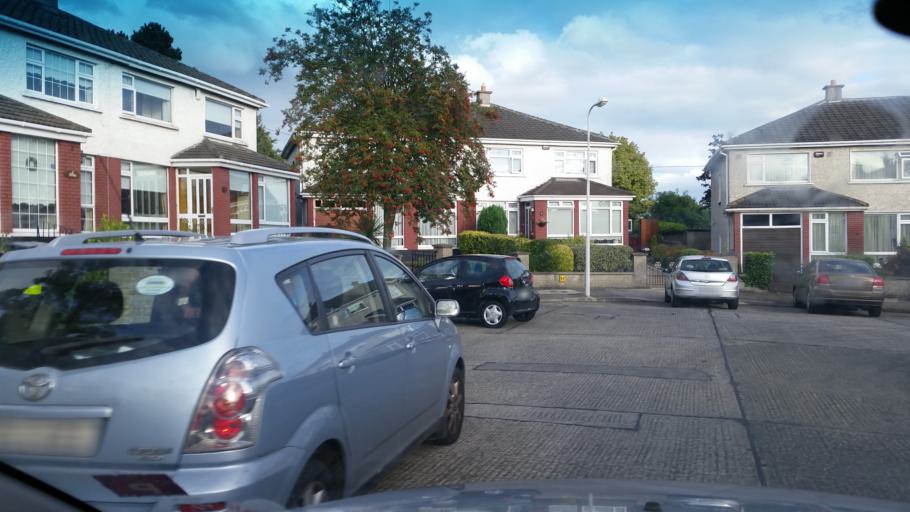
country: IE
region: Leinster
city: Drumcondra
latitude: 53.3796
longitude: -6.2508
